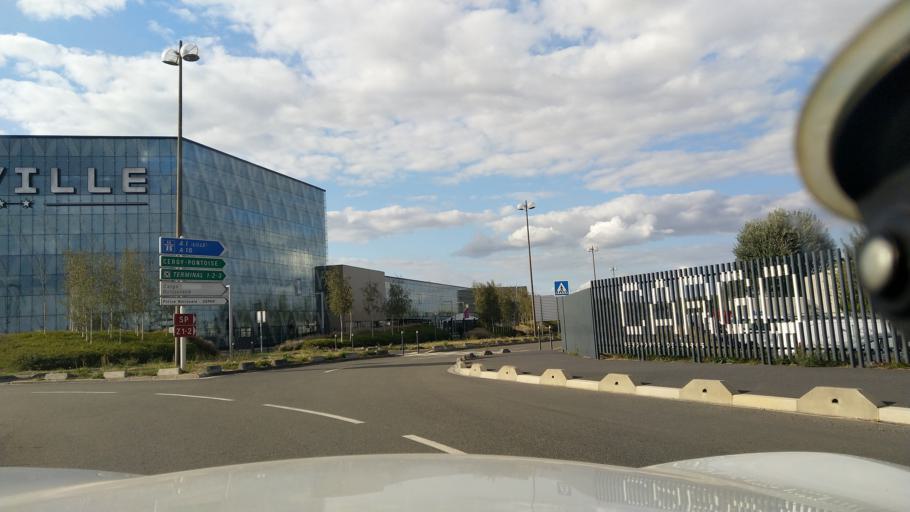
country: FR
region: Ile-de-France
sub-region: Departement du Val-d'Oise
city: Roissy-en-France
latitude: 48.9894
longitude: 2.5245
